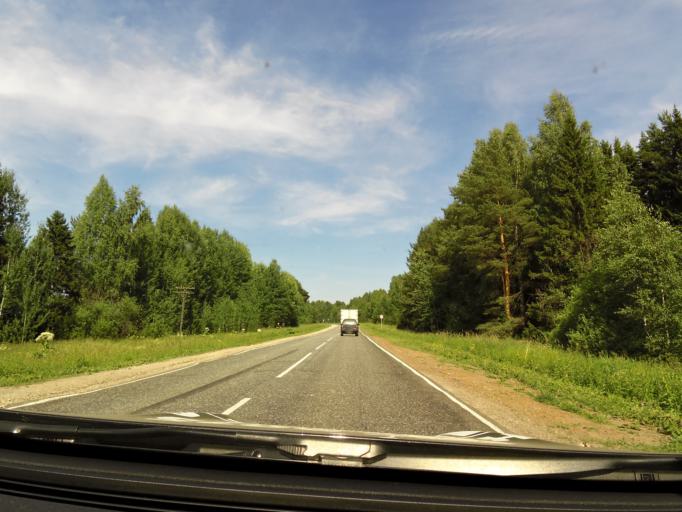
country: RU
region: Kirov
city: Slobodskoy
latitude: 58.7868
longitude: 50.5059
